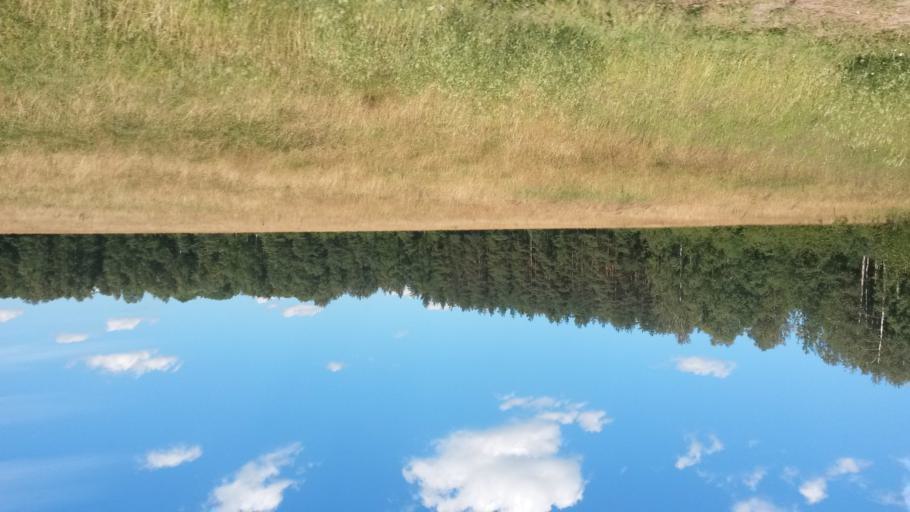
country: RU
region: Jaroslavl
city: Gavrilov-Yam
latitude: 57.4146
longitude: 39.9203
